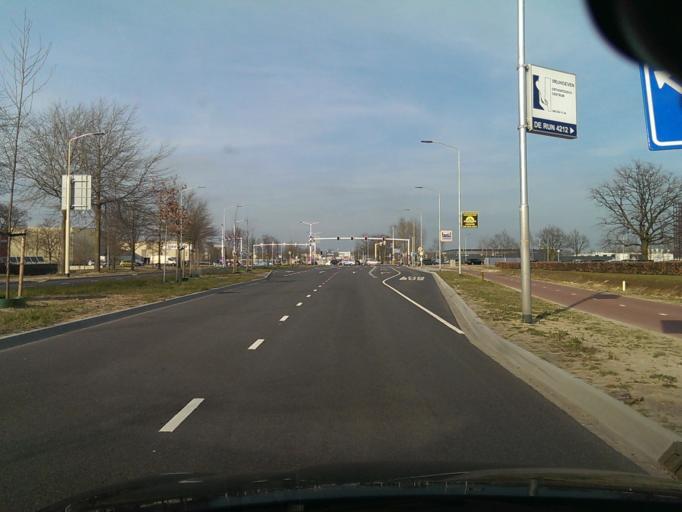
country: NL
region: North Brabant
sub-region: Gemeente Veldhoven
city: Veldhoven
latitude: 51.4074
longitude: 5.4160
